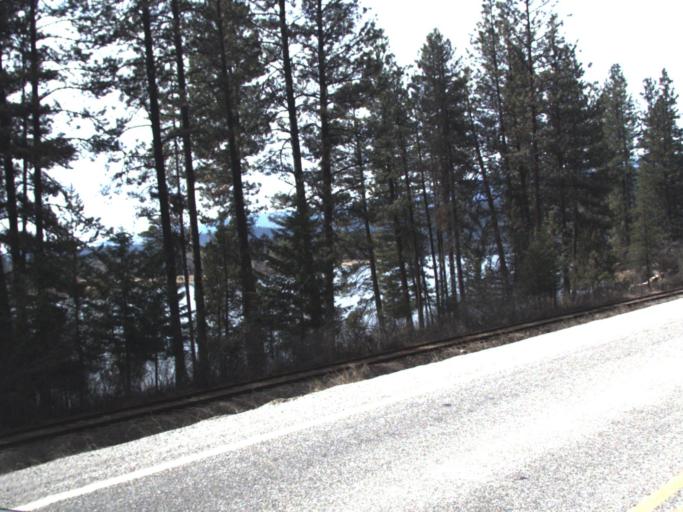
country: US
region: Washington
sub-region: Pend Oreille County
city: Newport
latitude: 48.4761
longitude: -117.2859
